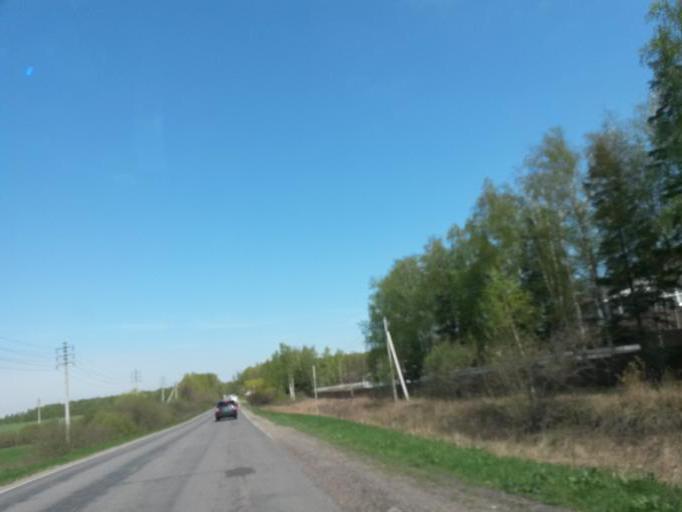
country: RU
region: Moskovskaya
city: L'vovskiy
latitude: 55.3234
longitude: 37.6118
